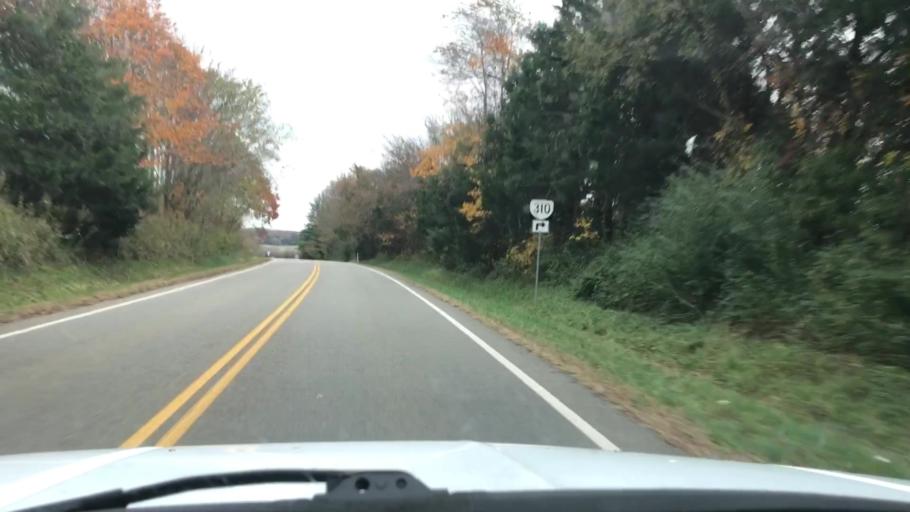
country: US
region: Virginia
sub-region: Goochland County
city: Goochland
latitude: 37.6486
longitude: -77.8376
